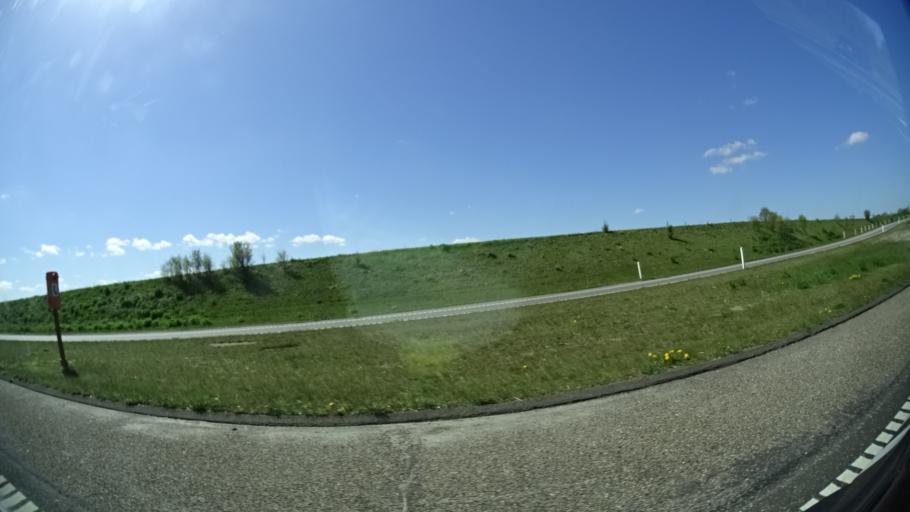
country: DK
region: Central Jutland
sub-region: Arhus Kommune
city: Trige
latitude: 56.3106
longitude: 10.1193
